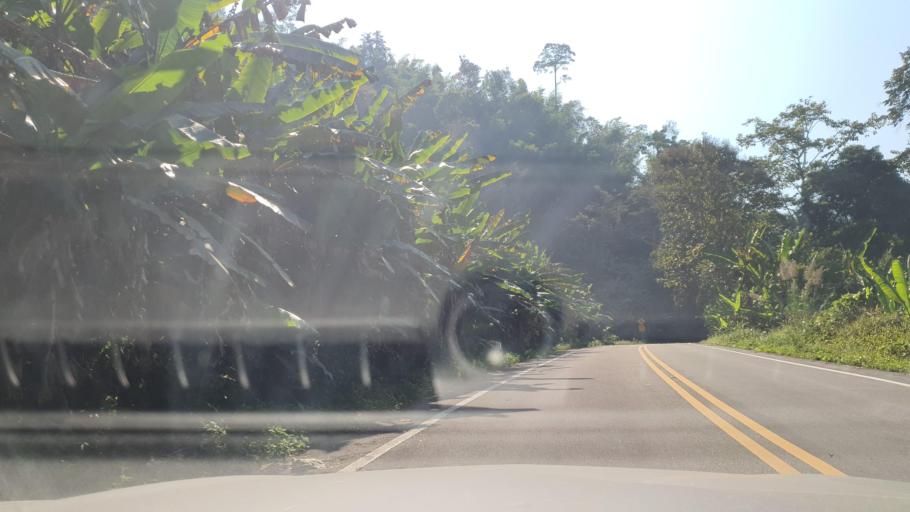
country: TH
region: Chiang Rai
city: Mae Lao
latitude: 19.8682
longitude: 99.6410
